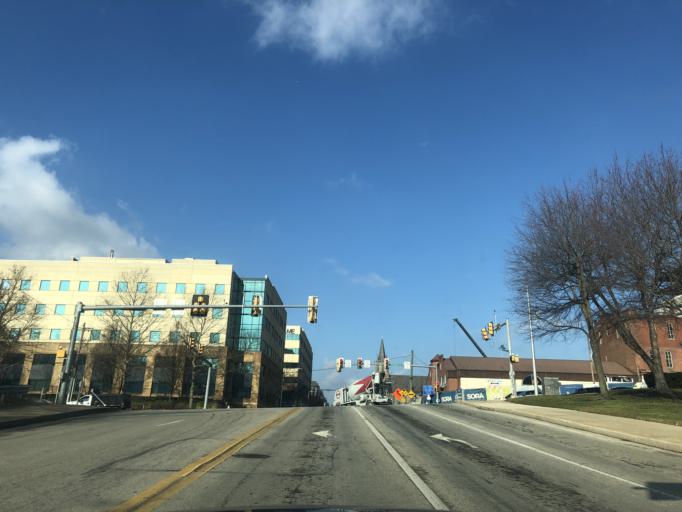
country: US
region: Pennsylvania
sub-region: Montgomery County
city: Conshohocken
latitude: 40.0725
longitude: -75.3068
